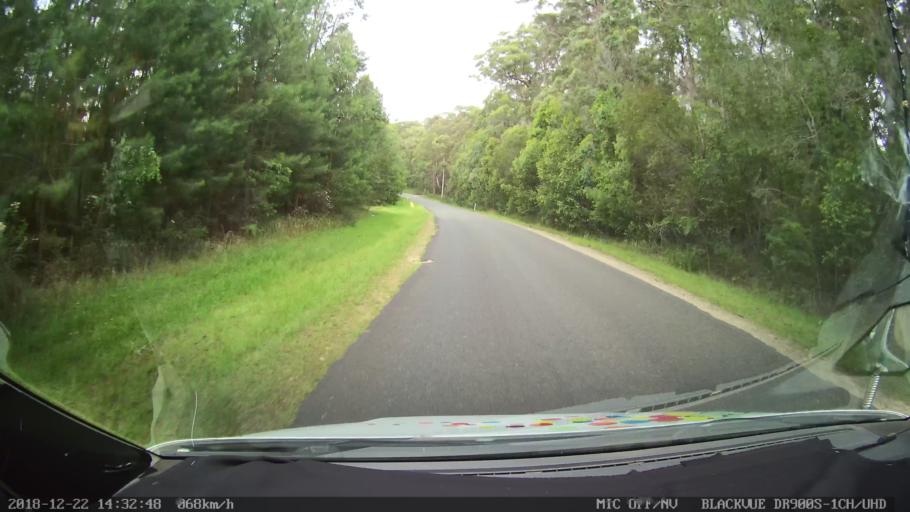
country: AU
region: New South Wales
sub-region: Bellingen
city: Dorrigo
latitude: -30.1072
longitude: 152.6242
